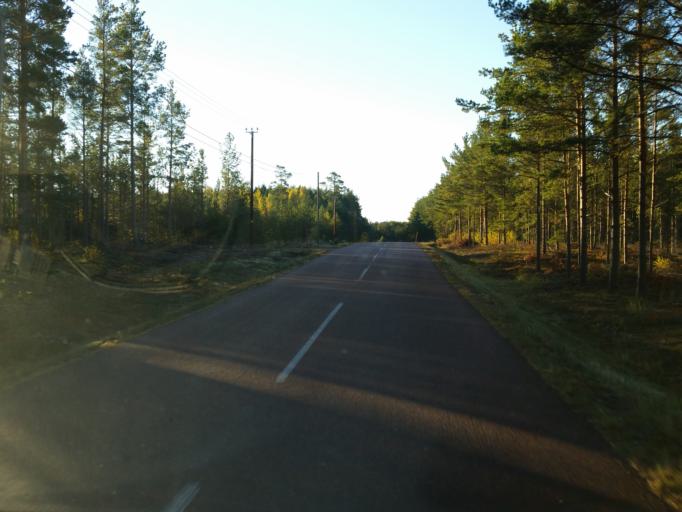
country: AX
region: Alands skaergard
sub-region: Vardoe
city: Vardoe
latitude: 60.2827
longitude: 20.3884
